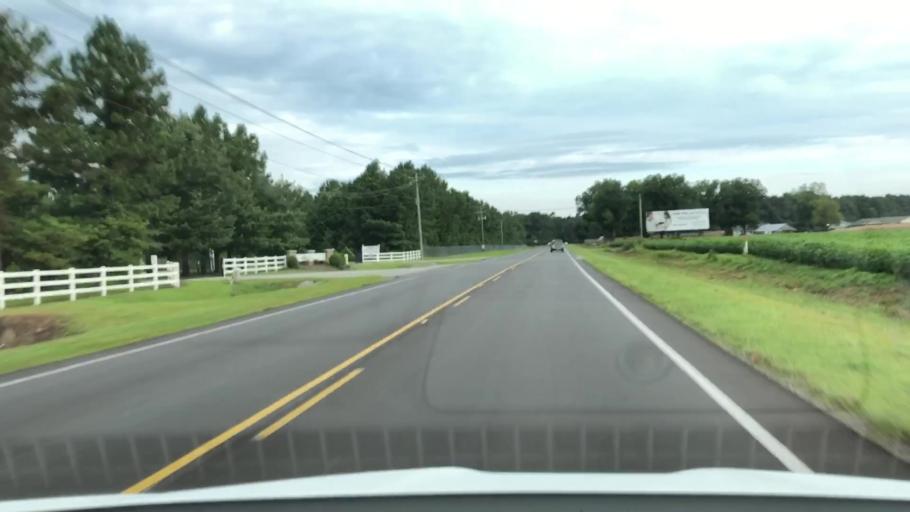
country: US
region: North Carolina
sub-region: Jones County
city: Maysville
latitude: 34.8832
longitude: -77.2094
